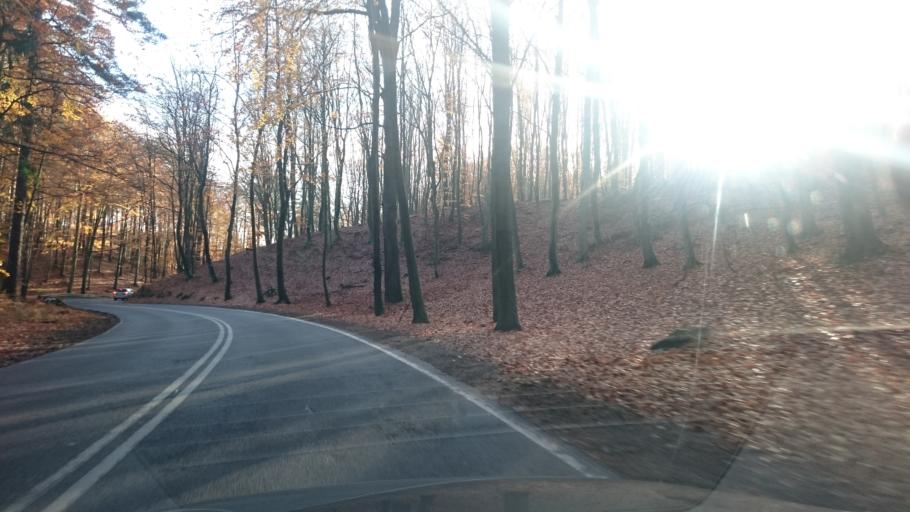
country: PL
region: Pomeranian Voivodeship
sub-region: Gdynia
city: Wielki Kack
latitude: 54.4584
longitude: 18.5100
